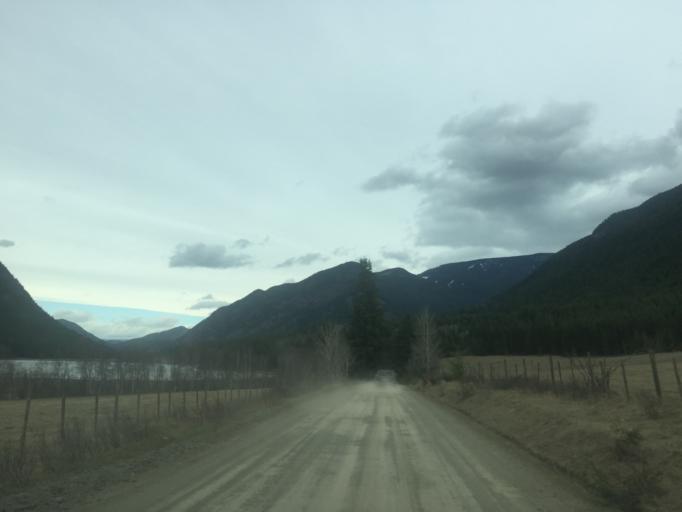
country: CA
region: British Columbia
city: Chase
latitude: 51.3808
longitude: -120.1281
